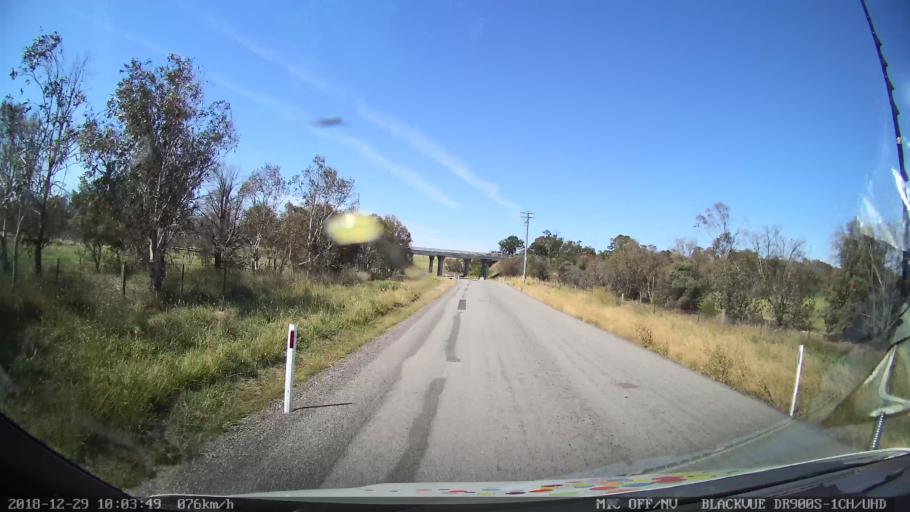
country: AU
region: New South Wales
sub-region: Goulburn Mulwaree
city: Goulburn
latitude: -34.8151
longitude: 149.4574
